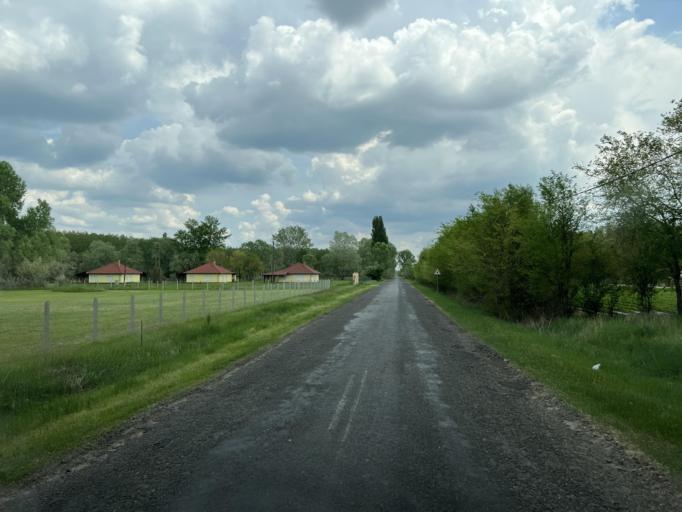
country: HU
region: Pest
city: Csemo
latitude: 47.0958
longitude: 19.7500
